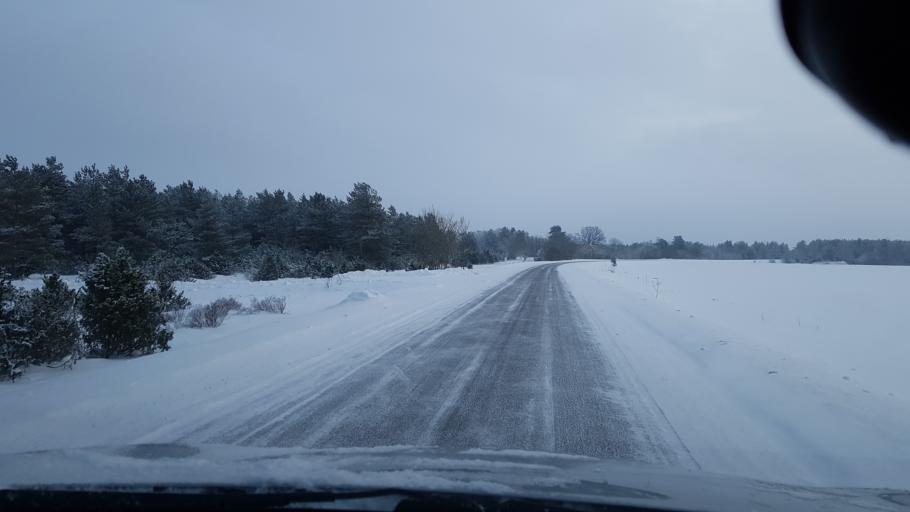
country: EE
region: Harju
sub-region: Keila linn
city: Keila
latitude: 59.3570
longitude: 24.4234
